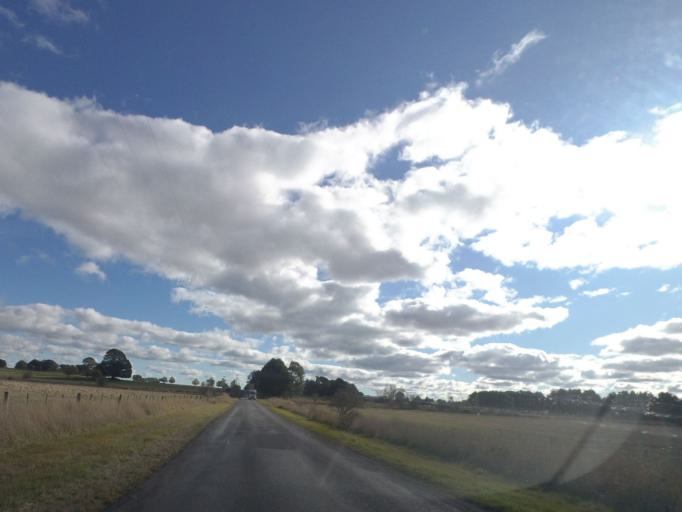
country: AU
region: Victoria
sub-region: Mount Alexander
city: Castlemaine
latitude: -37.2521
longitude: 144.4081
